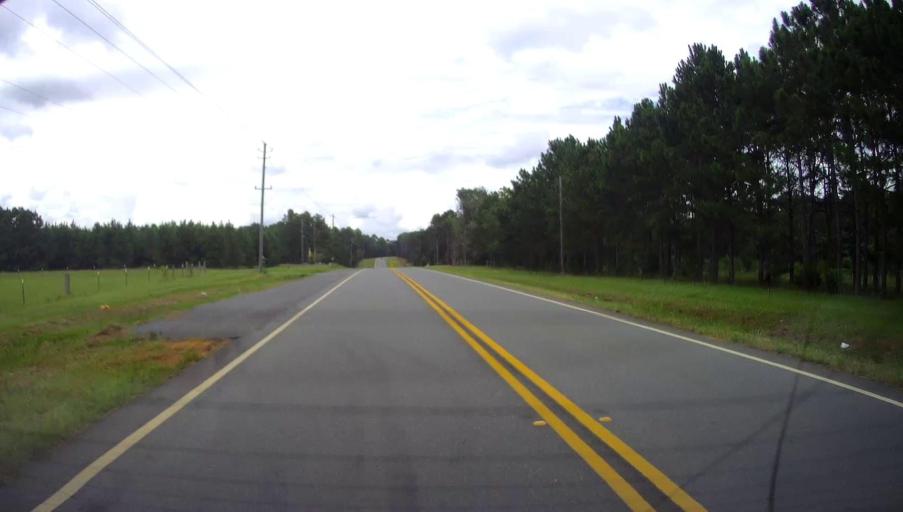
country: US
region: Georgia
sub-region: Schley County
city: Ellaville
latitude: 32.2508
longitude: -84.2806
